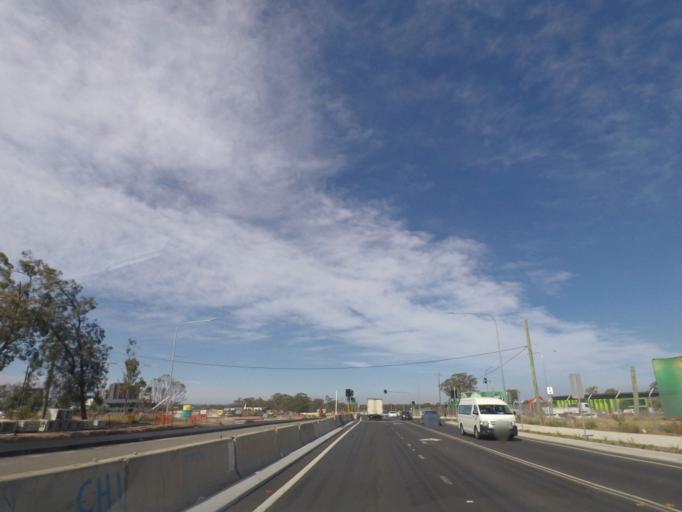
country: AU
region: New South Wales
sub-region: Campbelltown Municipality
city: Denham Court
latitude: -33.9750
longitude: 150.8558
